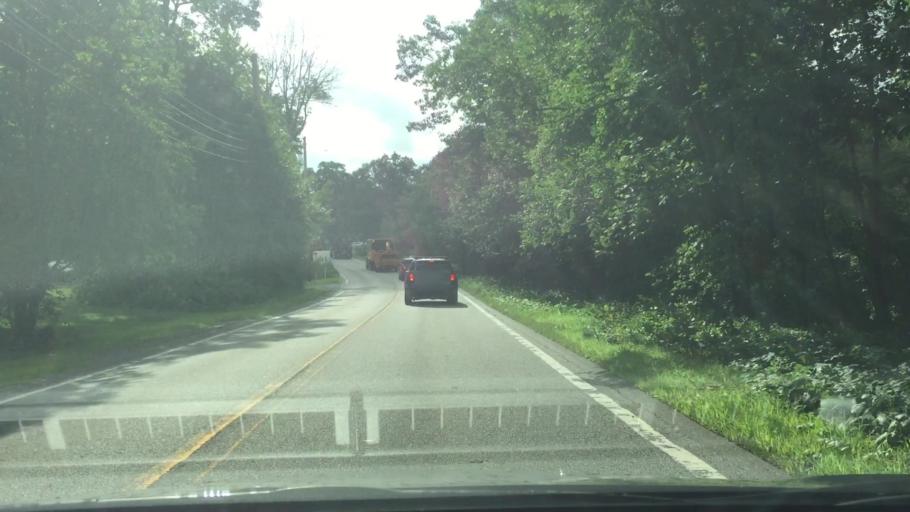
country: US
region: Massachusetts
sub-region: Middlesex County
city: Stow
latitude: 42.4823
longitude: -71.5164
